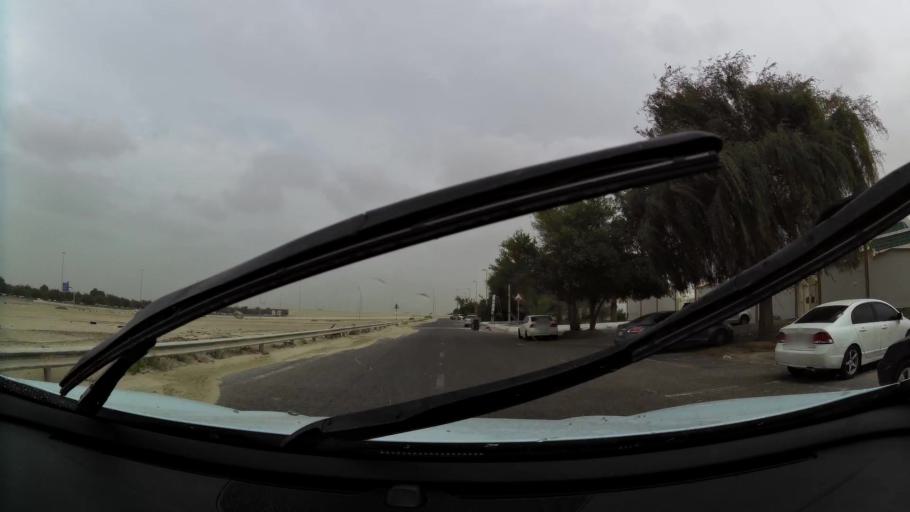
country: AE
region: Abu Dhabi
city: Abu Dhabi
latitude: 24.3636
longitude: 54.6543
